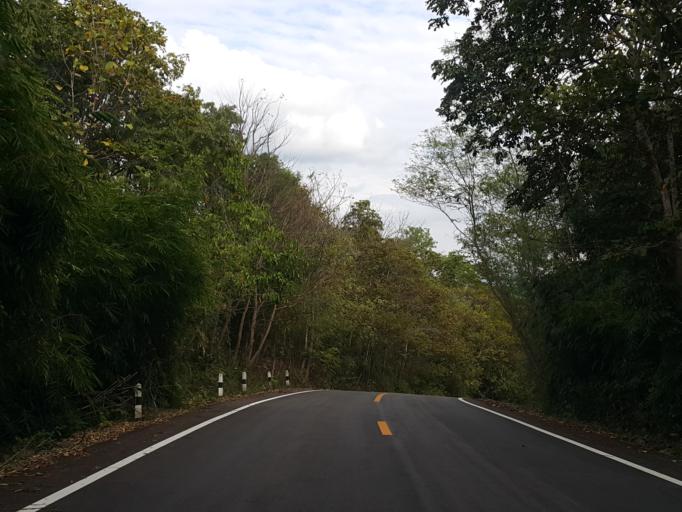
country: TH
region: Lampang
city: Chae Hom
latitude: 18.6534
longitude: 99.5272
